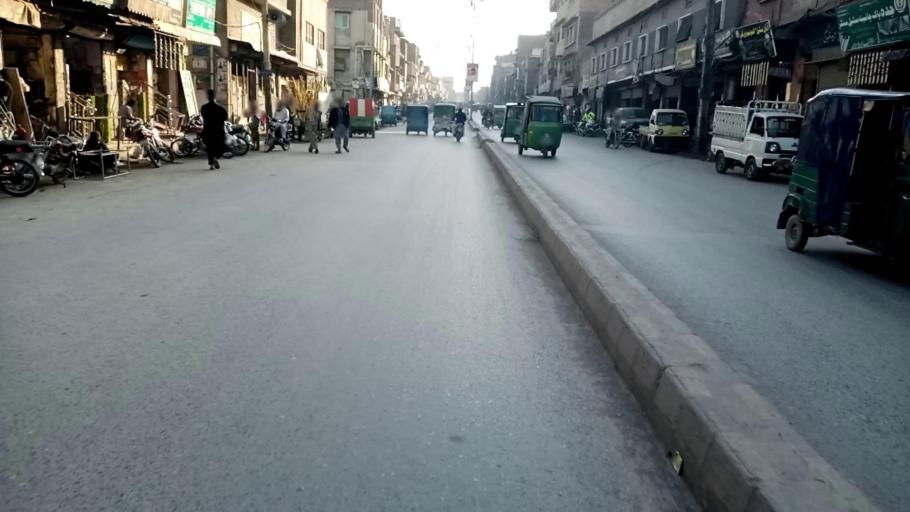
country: PK
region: Khyber Pakhtunkhwa
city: Peshawar
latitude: 34.0097
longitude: 71.5852
